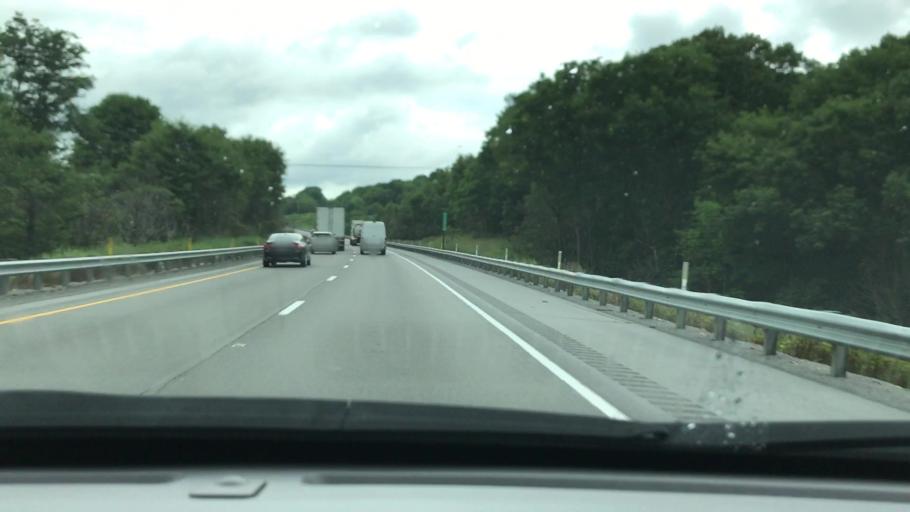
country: US
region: Pennsylvania
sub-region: Clearfield County
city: Clearfield
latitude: 41.0562
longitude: -78.4350
